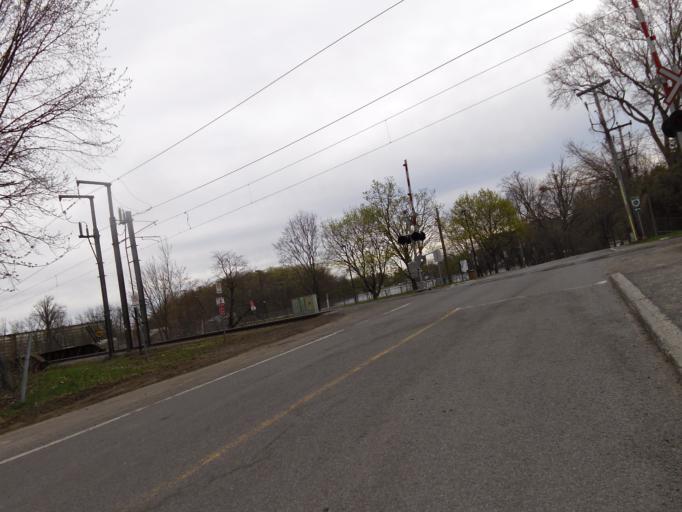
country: CA
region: Quebec
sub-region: Laurentides
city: Deux-Montagnes
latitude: 45.5315
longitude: -73.8814
